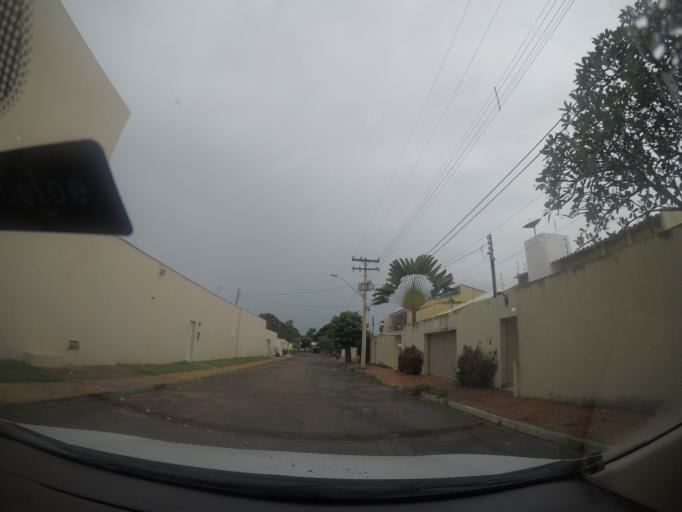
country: BR
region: Goias
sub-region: Goiania
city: Goiania
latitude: -16.6470
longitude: -49.2355
